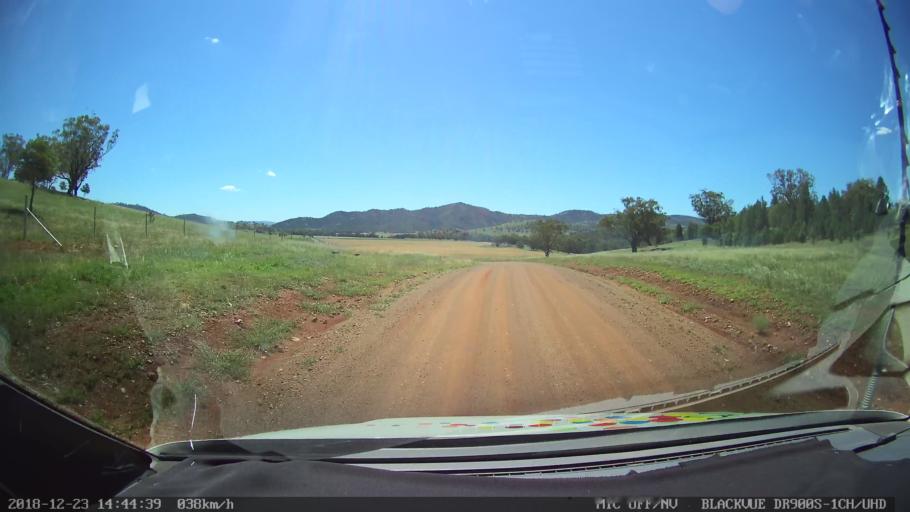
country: AU
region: New South Wales
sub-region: Tamworth Municipality
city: Manilla
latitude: -30.6460
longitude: 150.8945
